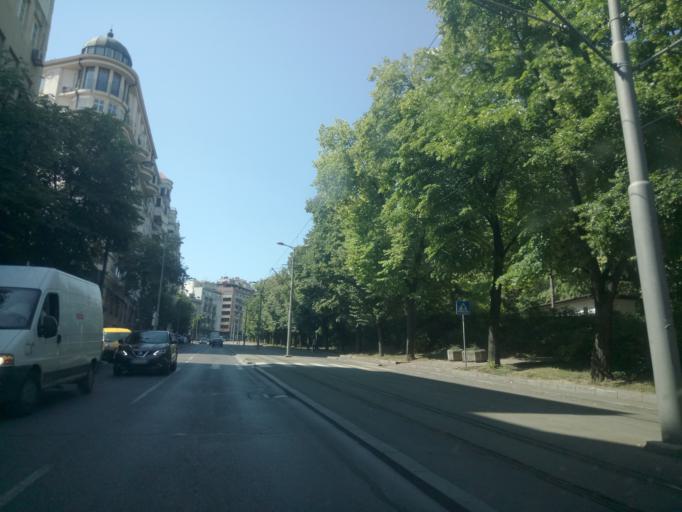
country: RS
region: Central Serbia
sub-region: Belgrade
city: Stari Grad
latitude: 44.8243
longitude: 20.4557
